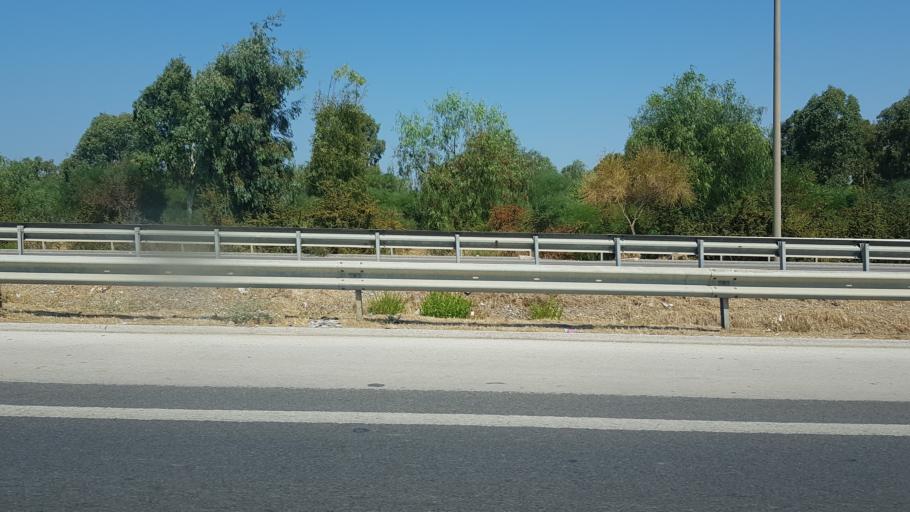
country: TR
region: Izmir
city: Karsiyaka
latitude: 38.3979
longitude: 27.0622
